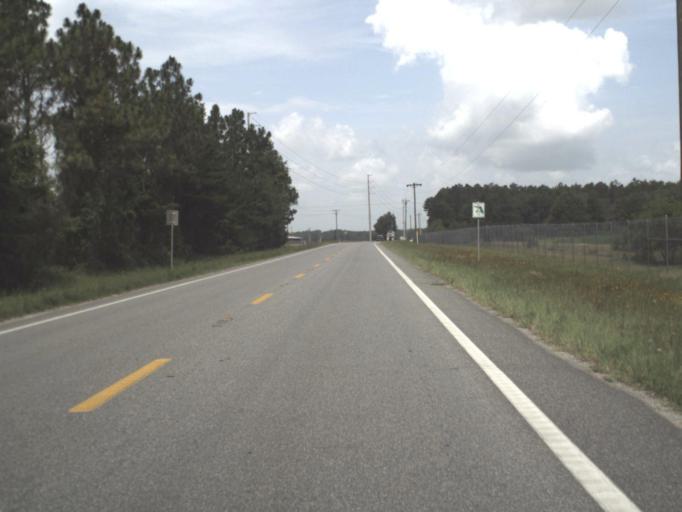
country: US
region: Florida
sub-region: Madison County
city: Madison
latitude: 30.4037
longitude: -83.2322
